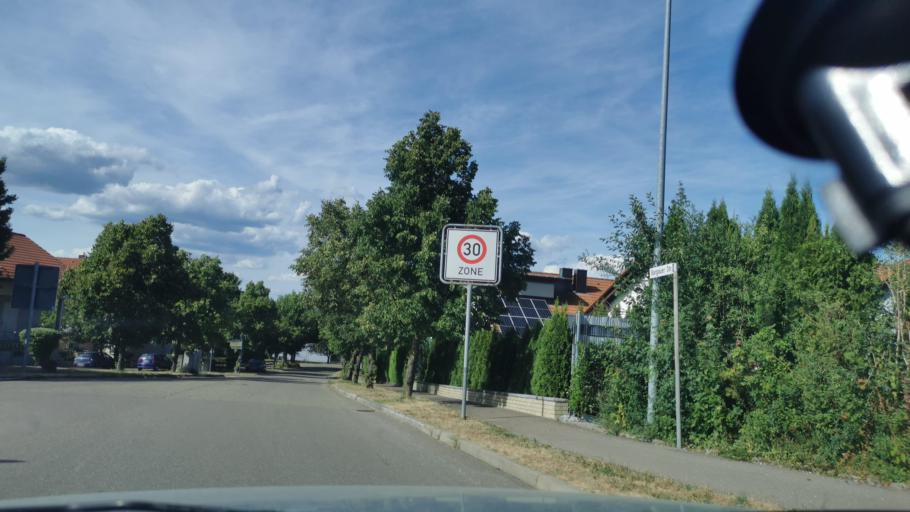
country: DE
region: Baden-Wuerttemberg
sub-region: Regierungsbezirk Stuttgart
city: Heubach
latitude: 48.7947
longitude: 9.9222
